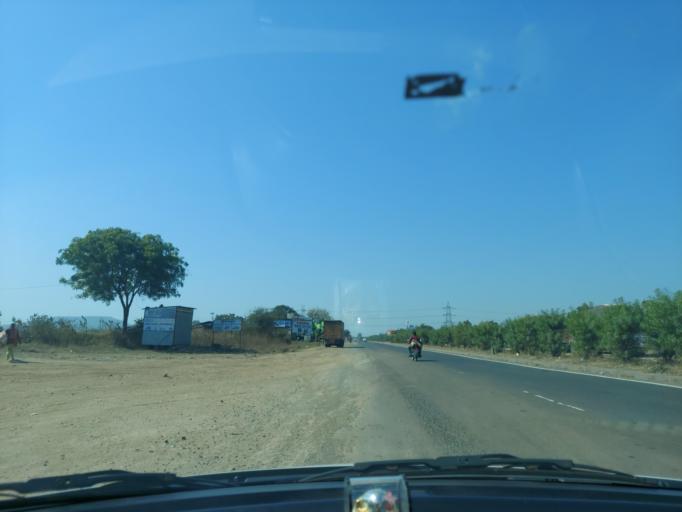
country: IN
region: Madhya Pradesh
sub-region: Indore
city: Manpur
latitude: 22.4207
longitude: 75.5991
